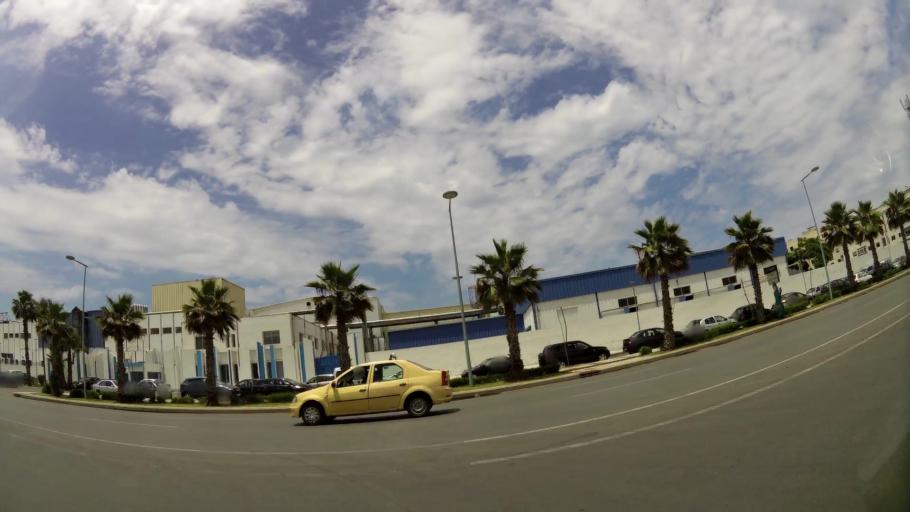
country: MA
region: Rabat-Sale-Zemmour-Zaer
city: Sale
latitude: 34.0554
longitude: -6.8083
